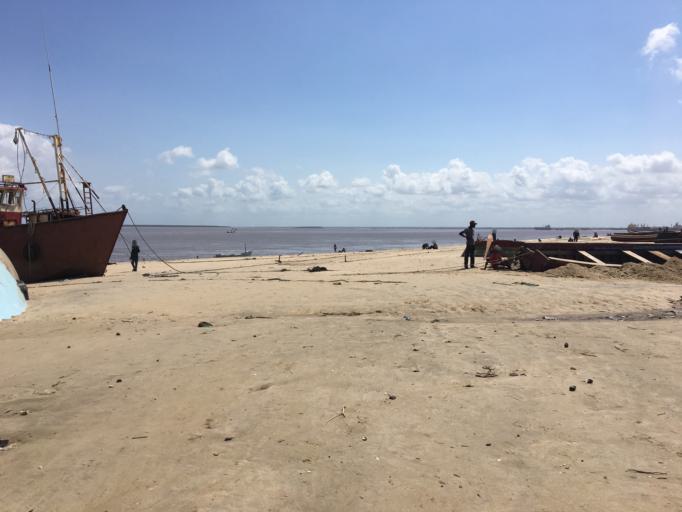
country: MZ
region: Sofala
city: Beira
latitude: -19.8344
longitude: 34.8310
